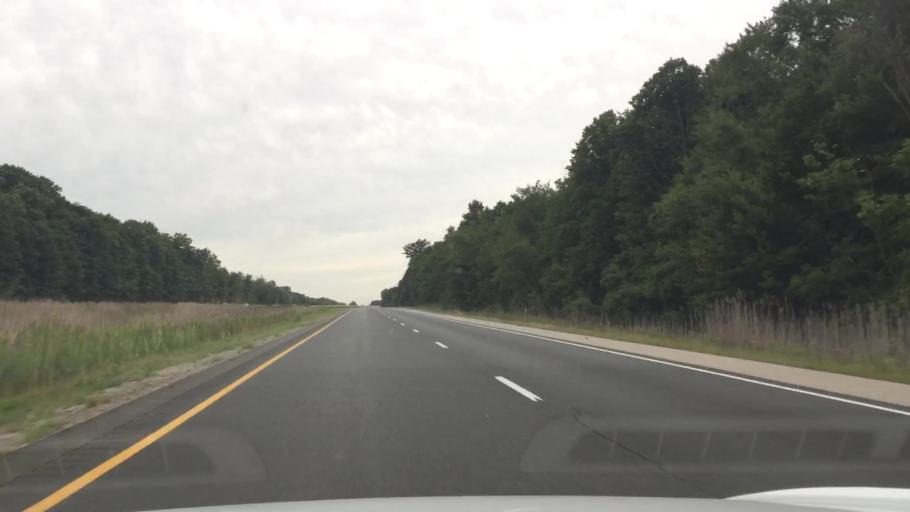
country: CA
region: Ontario
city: Lambton Shores
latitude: 42.9924
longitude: -81.8199
